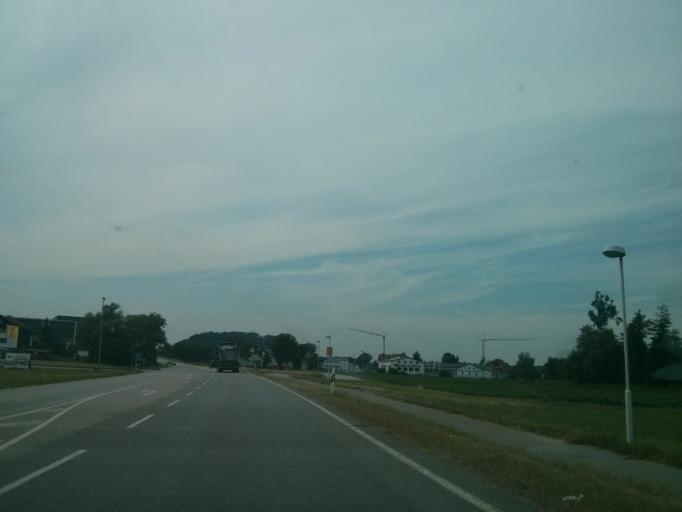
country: DE
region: Bavaria
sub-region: Lower Bavaria
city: Deggendorf
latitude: 48.8242
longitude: 12.9358
